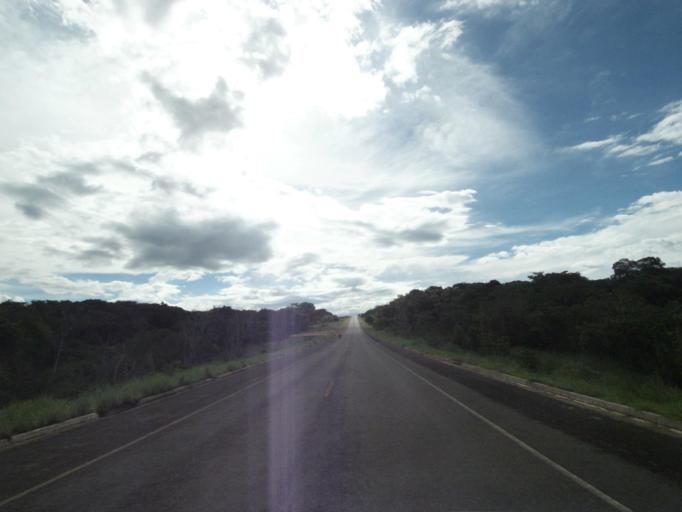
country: BR
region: Goias
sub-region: Jaragua
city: Jaragua
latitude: -15.8391
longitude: -49.2977
